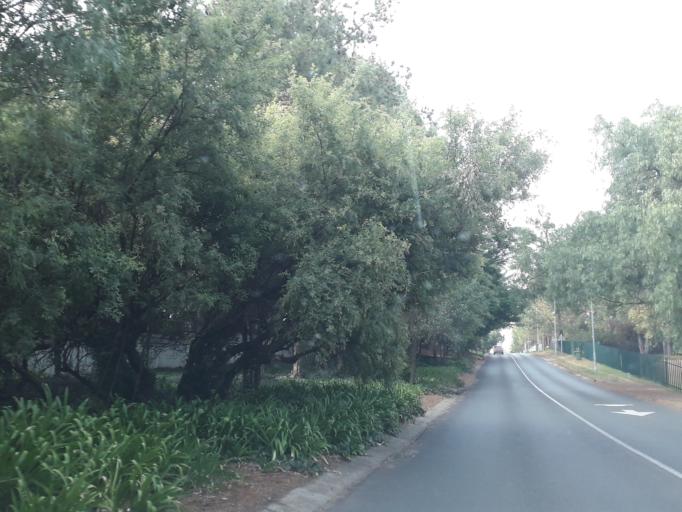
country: ZA
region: Gauteng
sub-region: City of Johannesburg Metropolitan Municipality
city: Johannesburg
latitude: -26.0820
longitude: 28.0419
